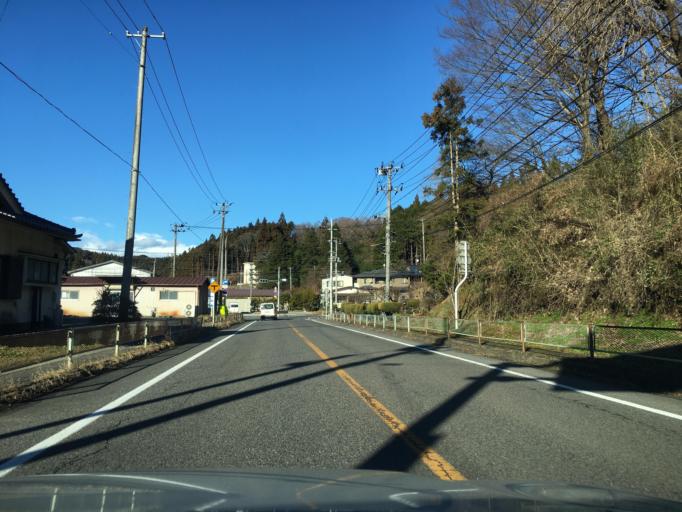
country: JP
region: Fukushima
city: Funehikimachi-funehiki
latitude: 37.2861
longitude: 140.6346
